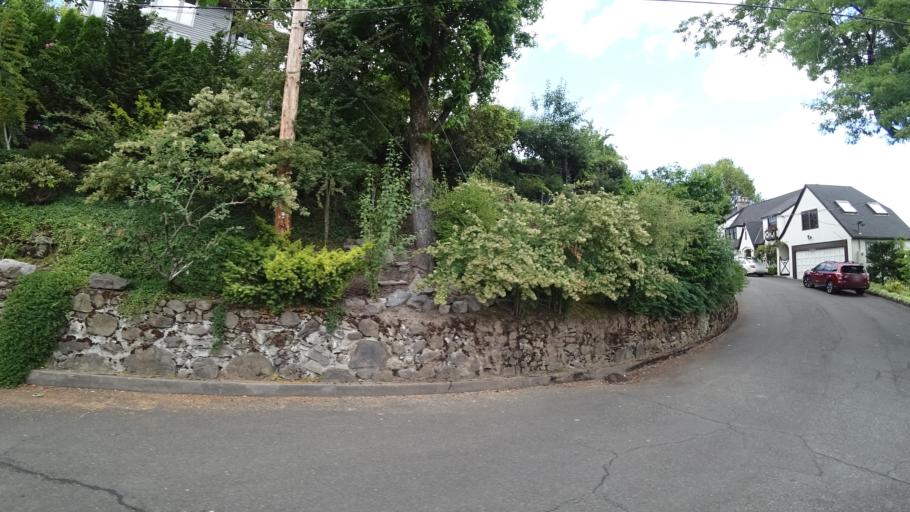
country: US
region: Oregon
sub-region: Multnomah County
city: Portland
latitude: 45.5254
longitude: -122.7065
